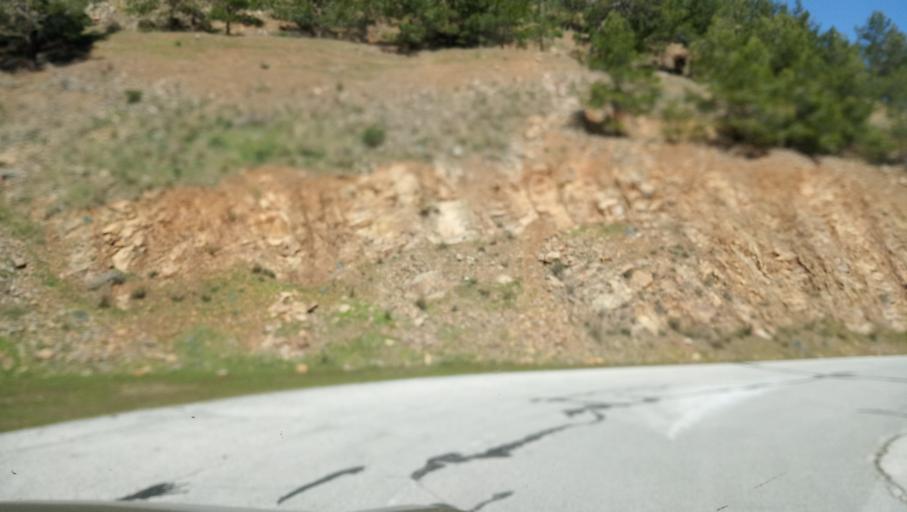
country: CY
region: Lefkosia
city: Lefka
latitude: 35.0829
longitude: 32.7798
